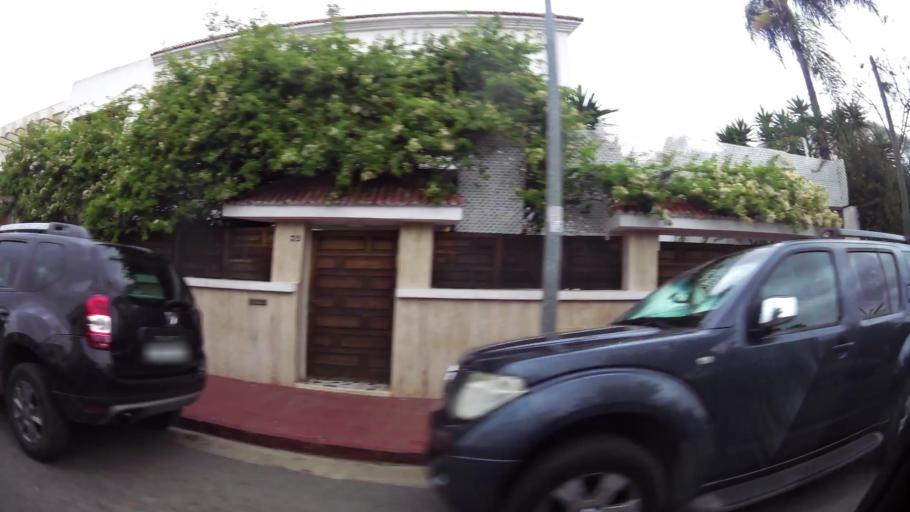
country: MA
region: Grand Casablanca
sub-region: Casablanca
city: Casablanca
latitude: 33.5708
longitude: -7.6592
